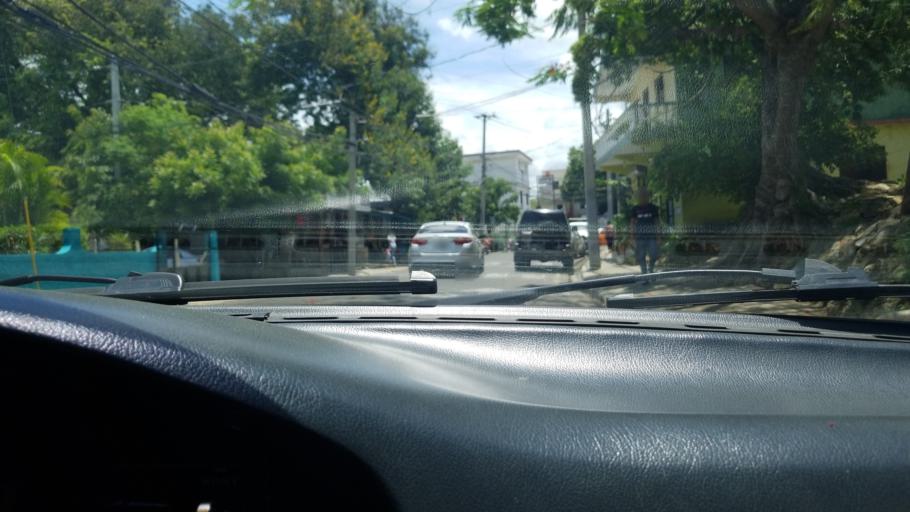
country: DO
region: Santiago
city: Santiago de los Caballeros
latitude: 19.4731
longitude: -70.6874
